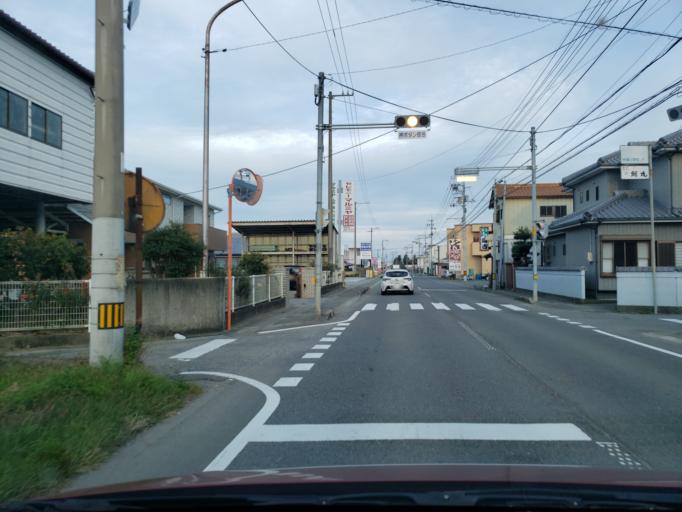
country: JP
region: Tokushima
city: Kamojimacho-jogejima
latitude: 34.0883
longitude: 134.2963
